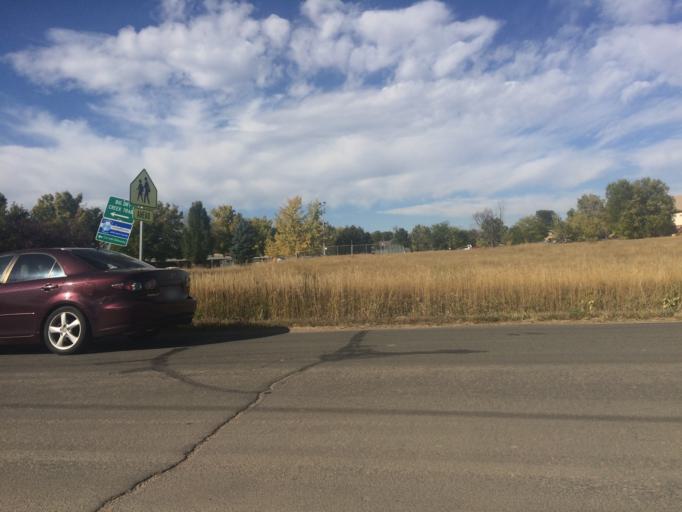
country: US
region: Colorado
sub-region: Broomfield County
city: Broomfield
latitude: 39.8762
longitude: -105.0837
